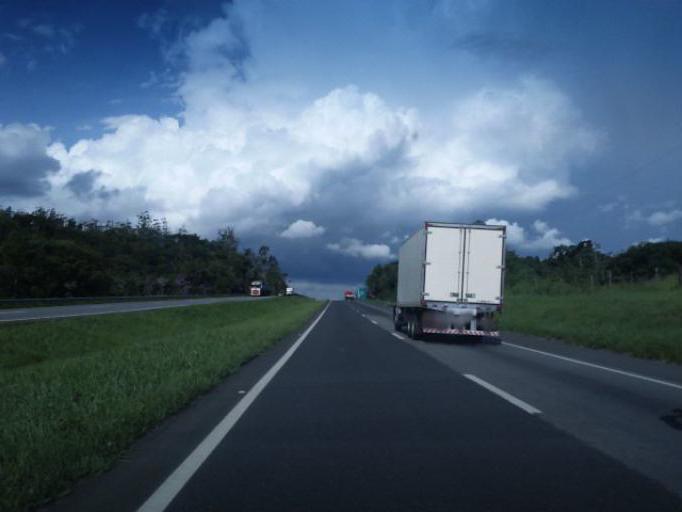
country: BR
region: Sao Paulo
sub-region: Juquia
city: Juquia
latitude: -24.3332
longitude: -47.5886
